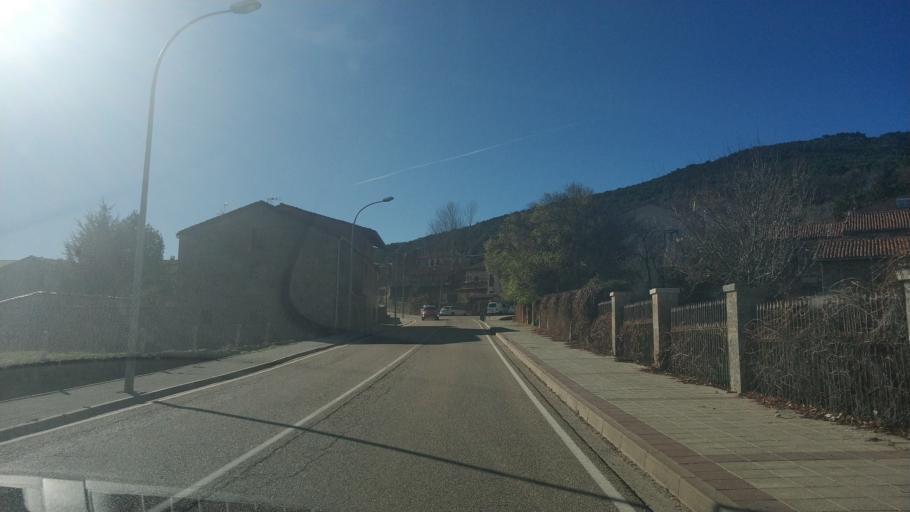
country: ES
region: Castille and Leon
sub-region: Provincia de Soria
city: Vinuesa
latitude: 41.9094
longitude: -2.7627
